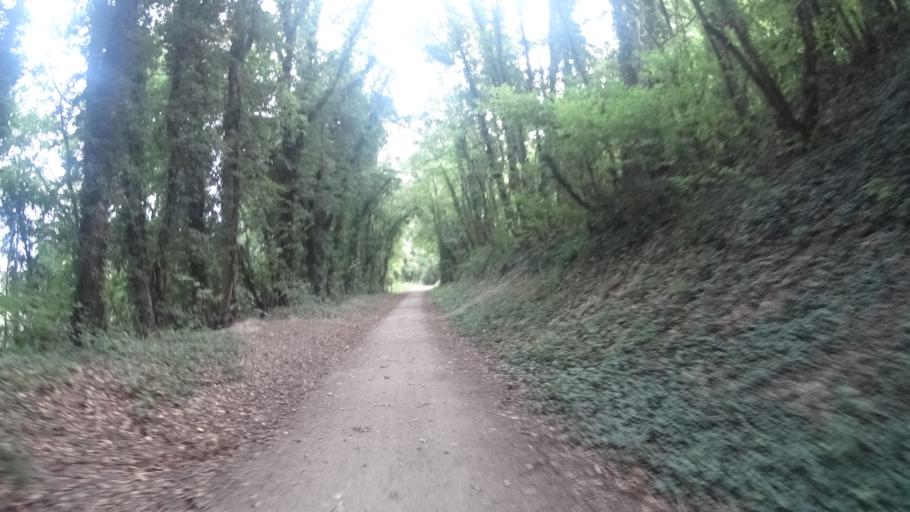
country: FR
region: Picardie
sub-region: Departement de l'Aisne
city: Origny-Sainte-Benoite
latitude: 49.8543
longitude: 3.4995
